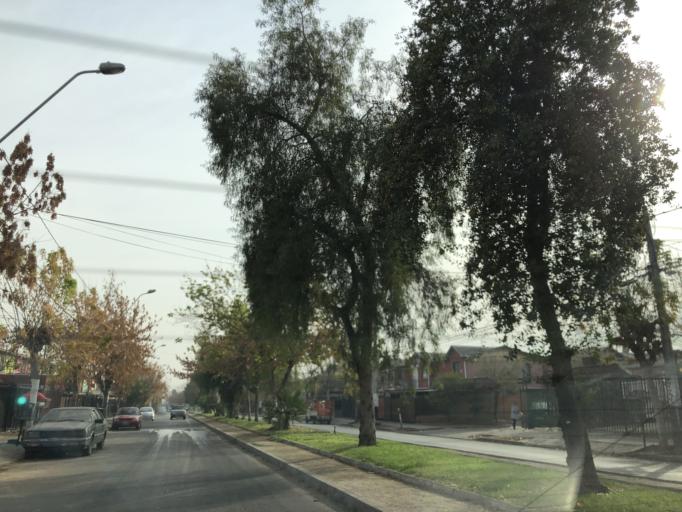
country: CL
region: Santiago Metropolitan
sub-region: Provincia de Cordillera
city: Puente Alto
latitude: -33.5860
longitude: -70.5553
